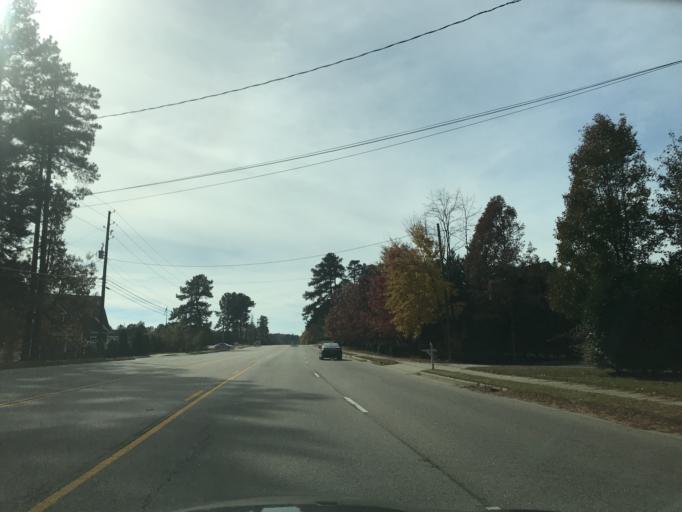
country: US
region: North Carolina
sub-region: Wake County
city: West Raleigh
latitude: 35.8295
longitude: -78.7018
